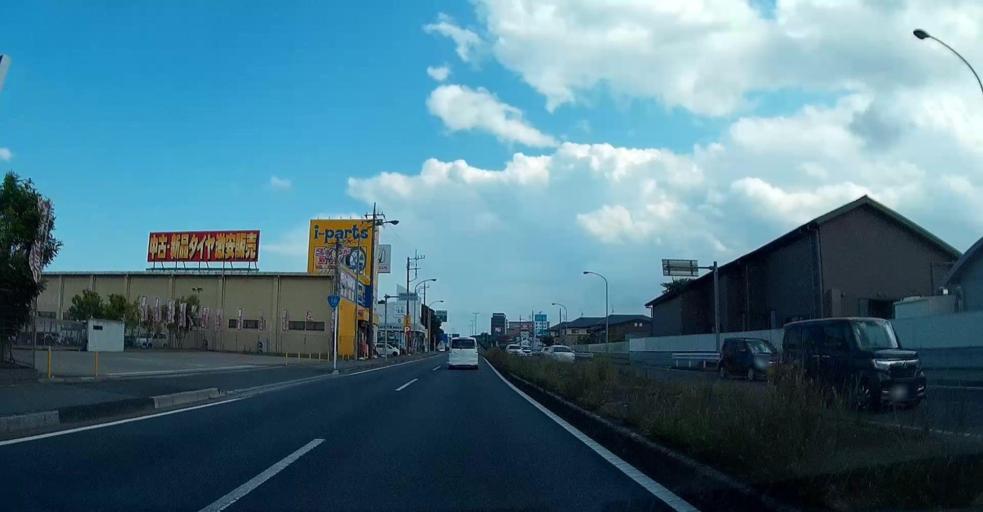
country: JP
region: Chiba
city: Noda
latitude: 35.9619
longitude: 139.8706
